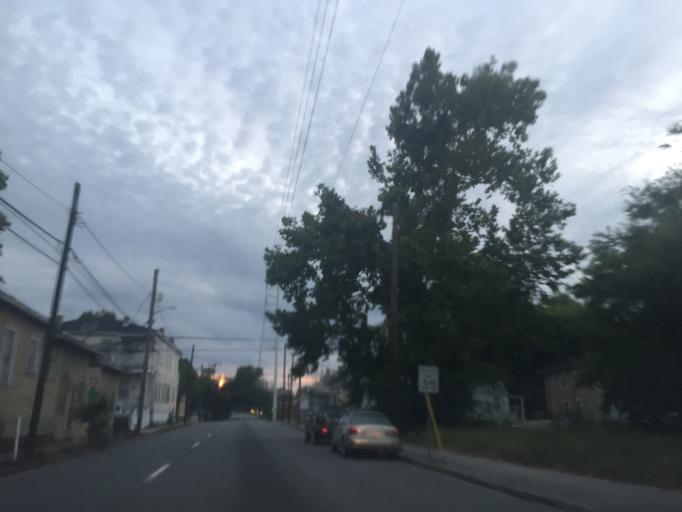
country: US
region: Georgia
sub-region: Chatham County
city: Savannah
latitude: 32.0621
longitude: -81.0903
